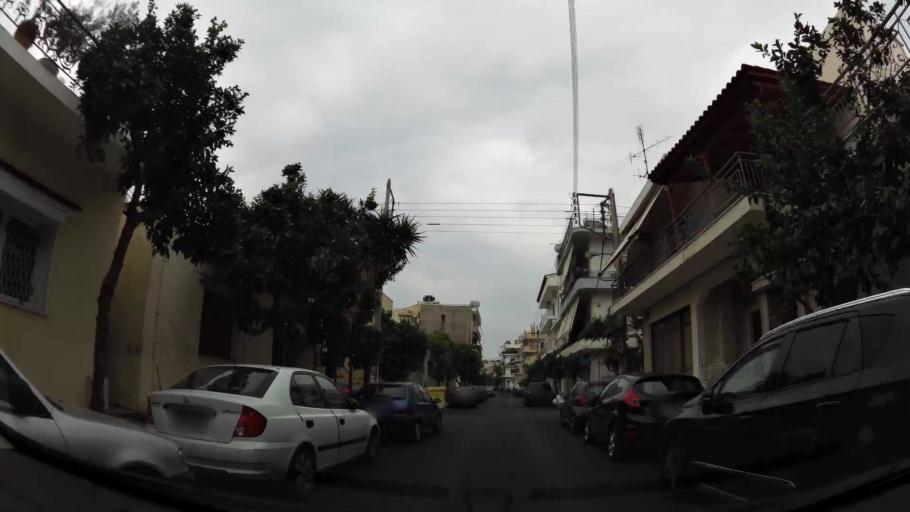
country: GR
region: Attica
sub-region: Nomarchia Athinas
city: Aigaleo
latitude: 37.9880
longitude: 23.6836
